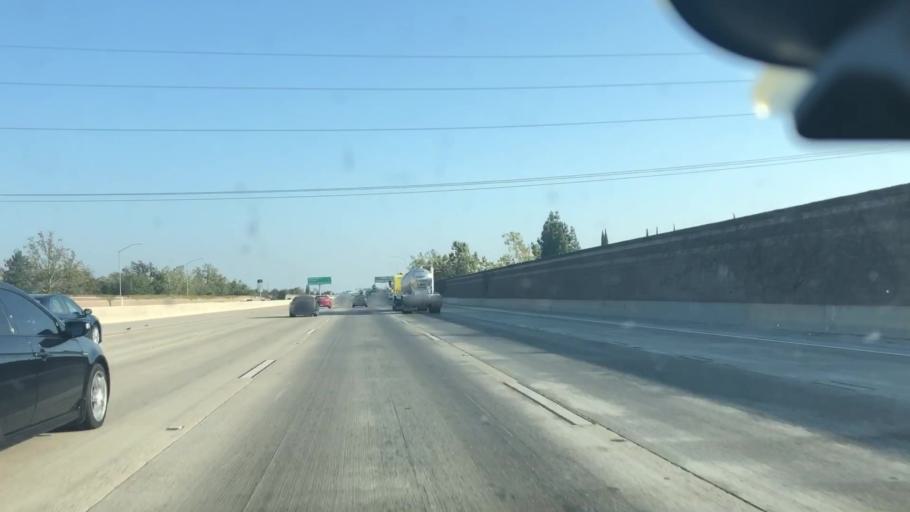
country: US
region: California
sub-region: San Joaquin County
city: Country Club
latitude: 37.9764
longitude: -121.3404
